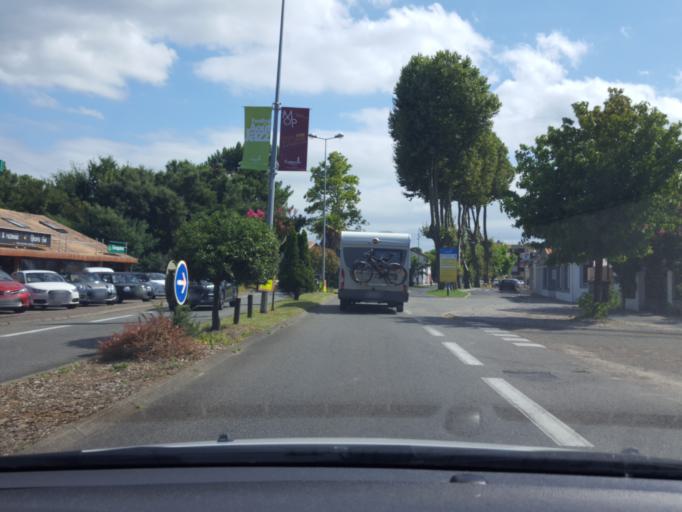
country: FR
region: Aquitaine
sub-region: Departement des Landes
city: Capbreton
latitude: 43.6422
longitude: -1.4258
